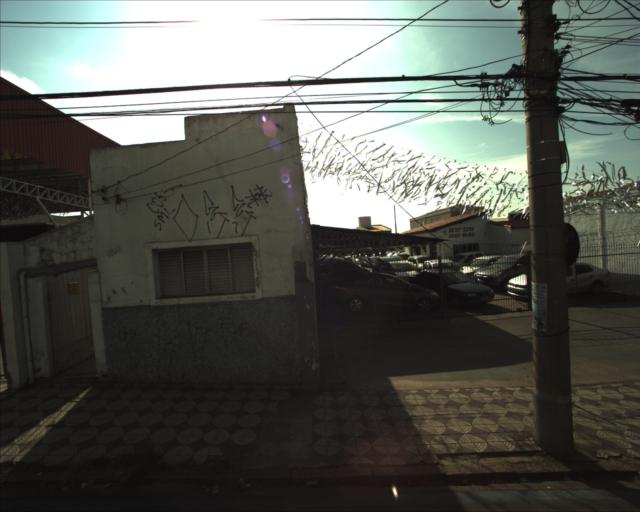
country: BR
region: Sao Paulo
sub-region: Sorocaba
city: Sorocaba
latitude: -23.4882
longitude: -47.4628
